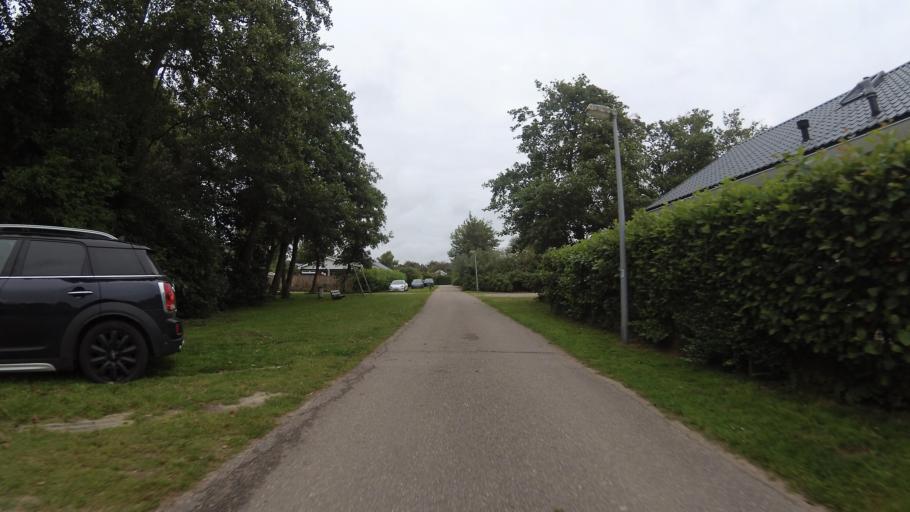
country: NL
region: North Holland
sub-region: Gemeente Den Helder
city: Den Helder
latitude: 52.8968
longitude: 4.7334
